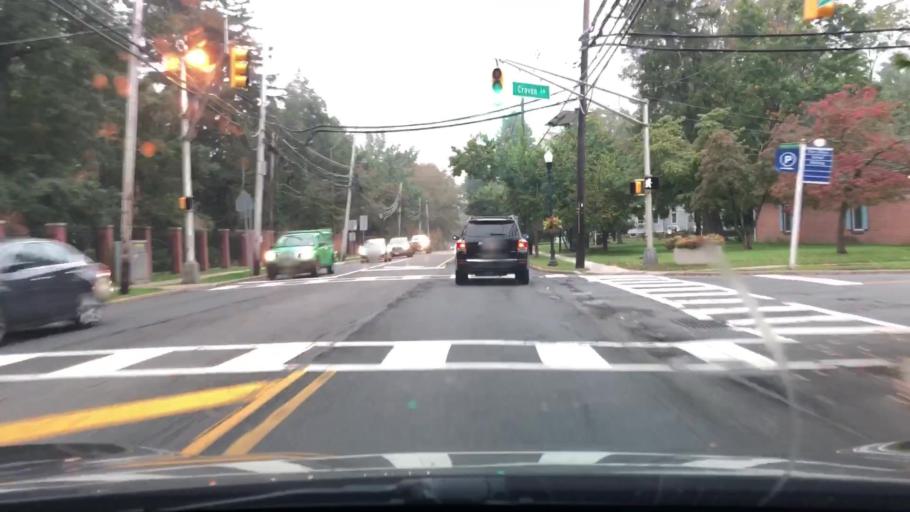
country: US
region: New Jersey
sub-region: Mercer County
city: Lawrenceville
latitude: 40.2962
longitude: -74.7310
